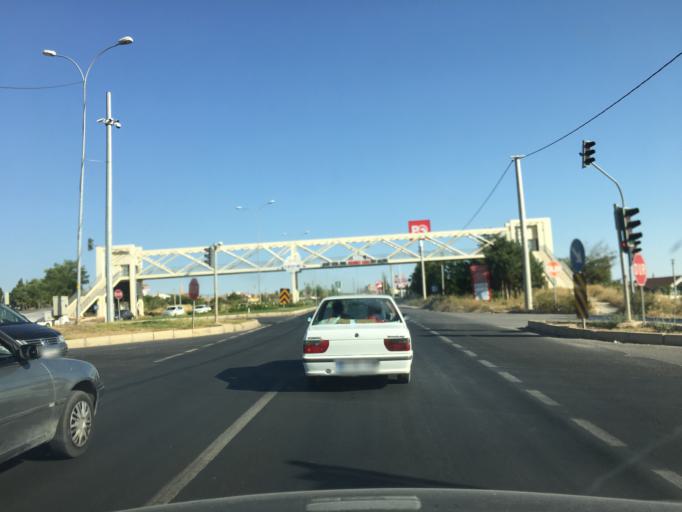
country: TR
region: Kirsehir
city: Kirsehir
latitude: 39.1341
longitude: 34.1861
